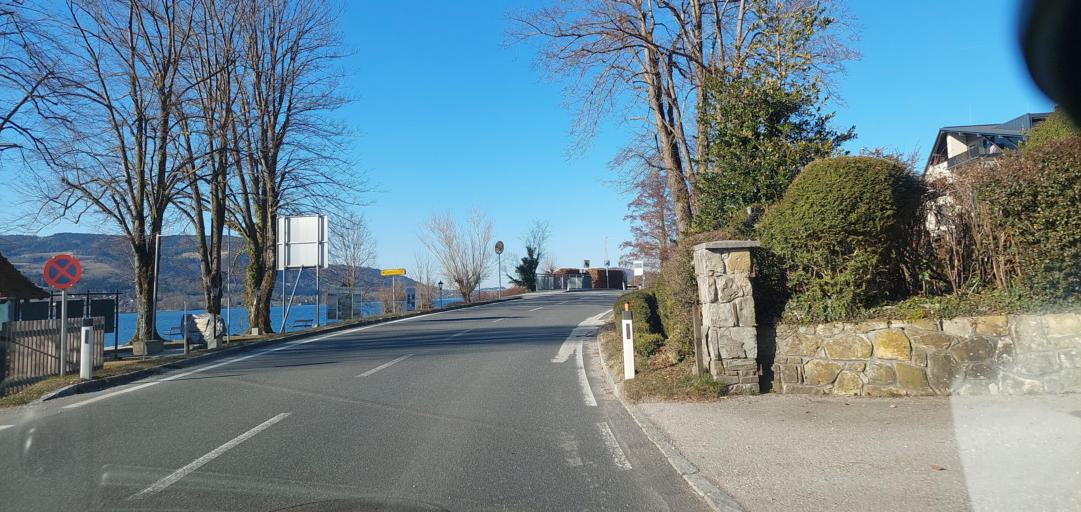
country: AT
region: Upper Austria
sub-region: Politischer Bezirk Vocklabruck
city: Steinbach am Attersee
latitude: 47.8300
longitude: 13.5457
